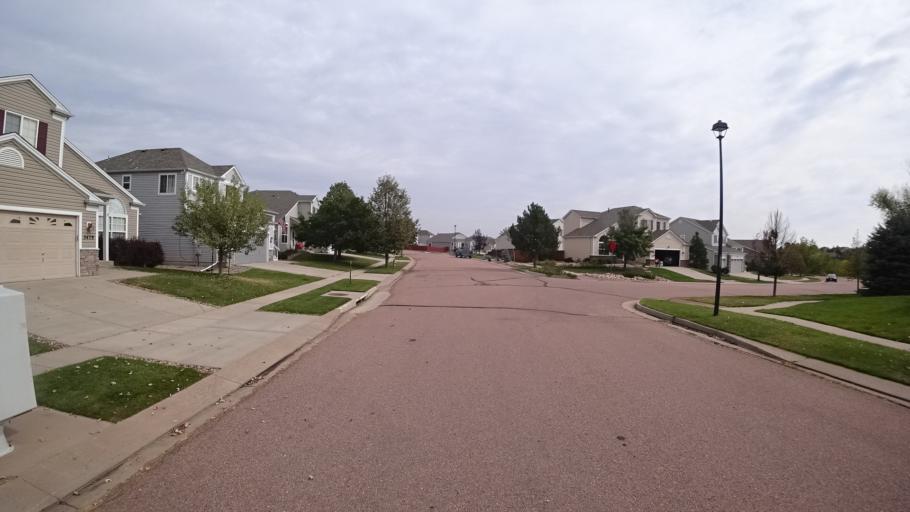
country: US
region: Colorado
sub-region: El Paso County
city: Cimarron Hills
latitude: 38.9129
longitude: -104.7036
